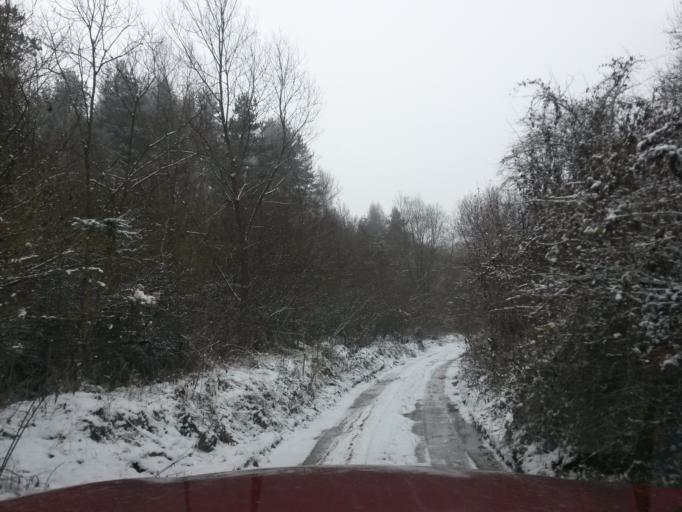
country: SK
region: Kosicky
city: Krompachy
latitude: 48.9836
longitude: 20.9903
